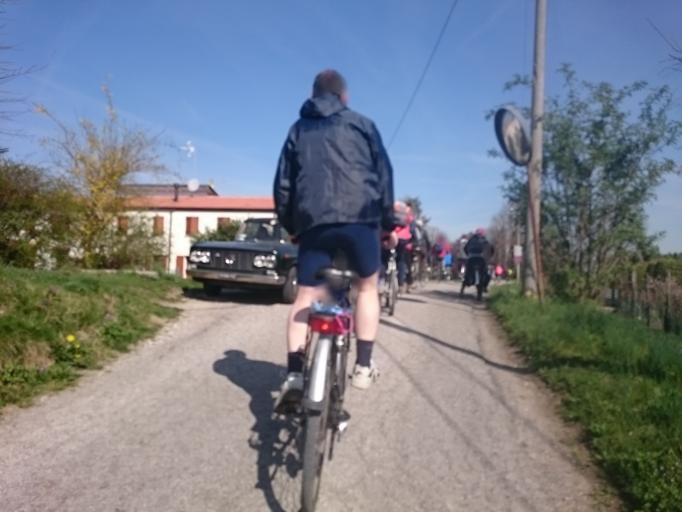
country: IT
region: Veneto
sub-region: Provincia di Padova
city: Sarmeola
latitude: 45.4189
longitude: 11.8283
